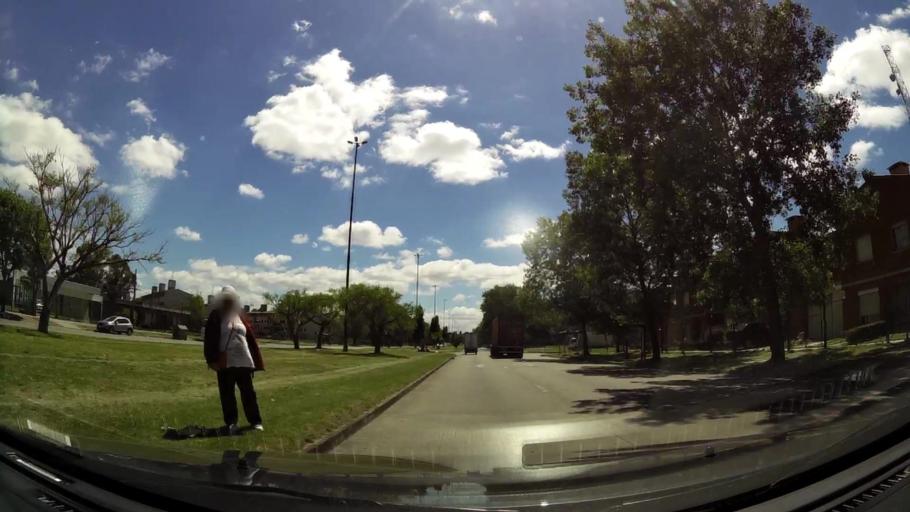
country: UY
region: Montevideo
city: Montevideo
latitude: -34.8614
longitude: -56.1477
